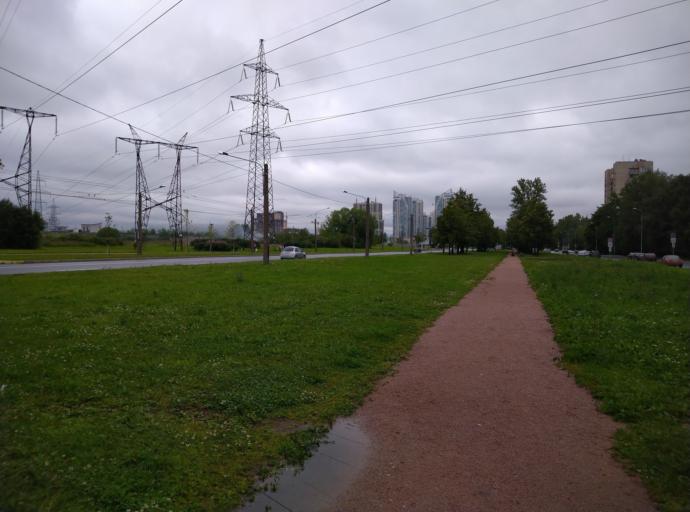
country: RU
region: St.-Petersburg
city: Kupchino
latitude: 59.8455
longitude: 30.3560
